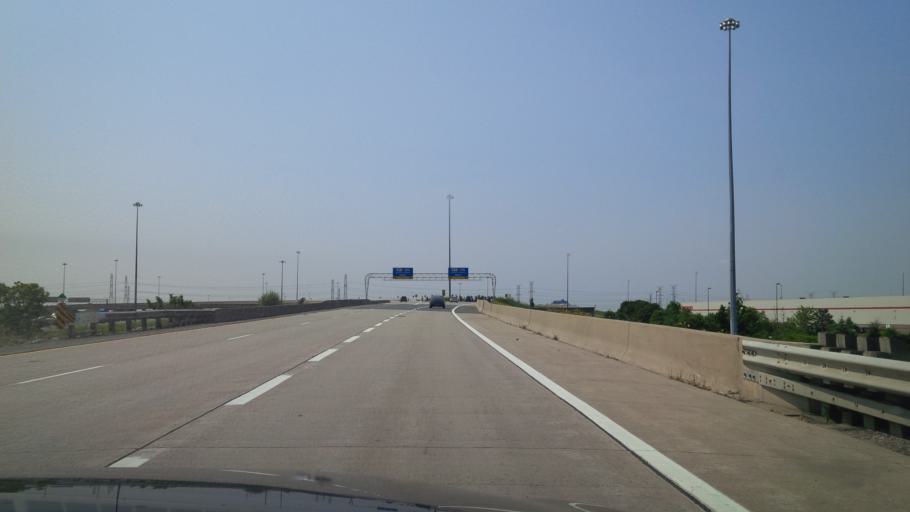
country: CA
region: Ontario
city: Concord
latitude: 43.7880
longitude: -79.5396
